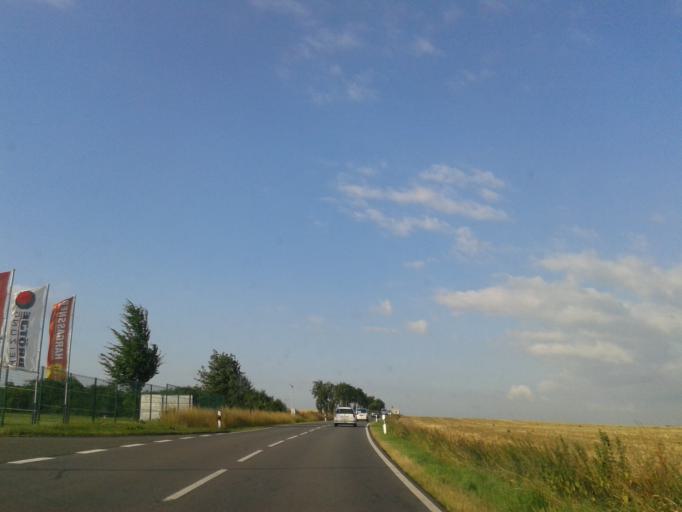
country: DE
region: Saxony
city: Niederschona
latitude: 50.9940
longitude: 13.4531
